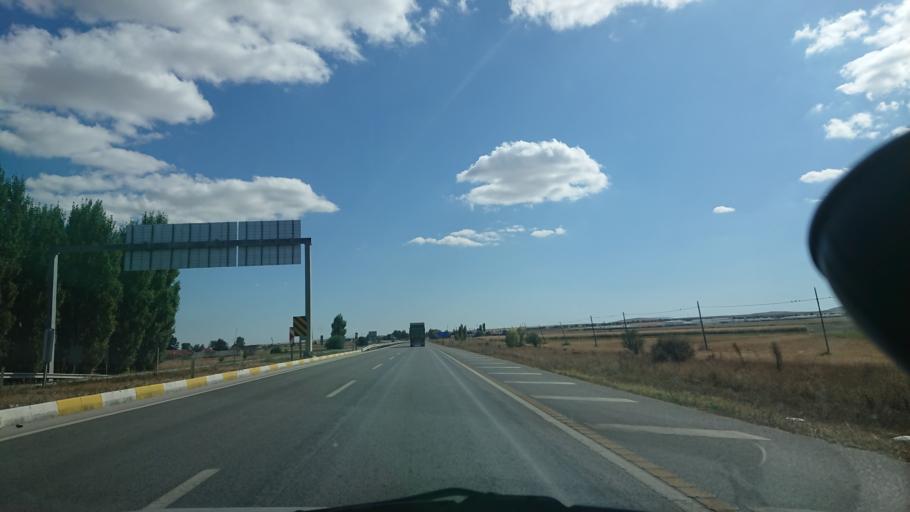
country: TR
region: Eskisehir
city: Mahmudiye
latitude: 39.5689
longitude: 30.9137
